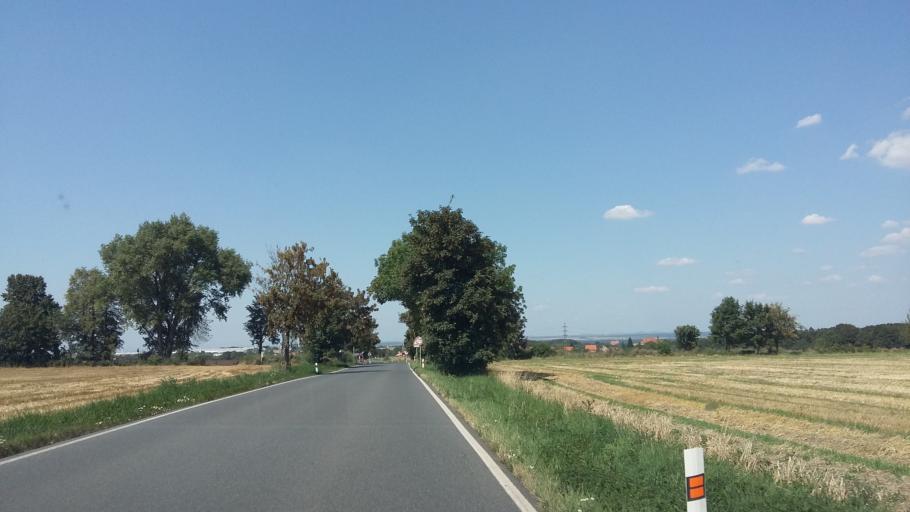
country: CZ
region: Central Bohemia
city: Zelenec
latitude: 50.1541
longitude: 14.6861
